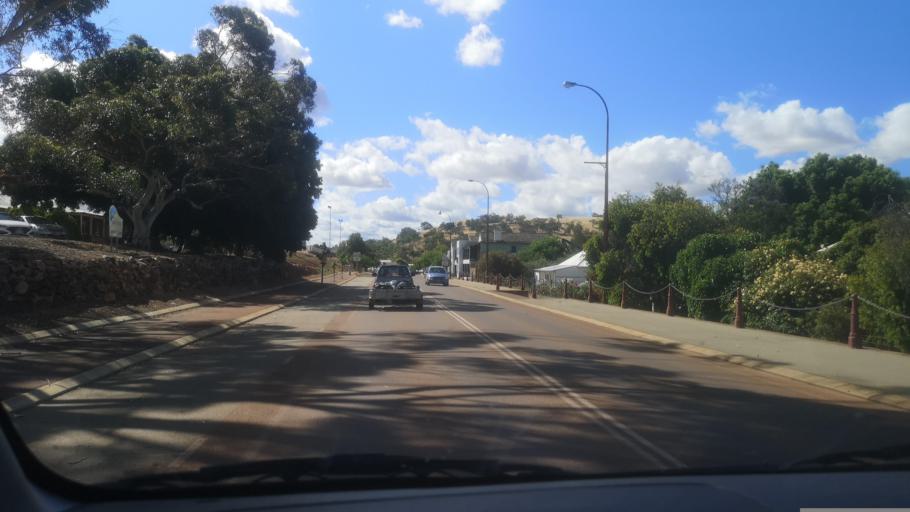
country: AU
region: Western Australia
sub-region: Toodyay
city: Toodyay
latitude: -31.5524
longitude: 116.4716
